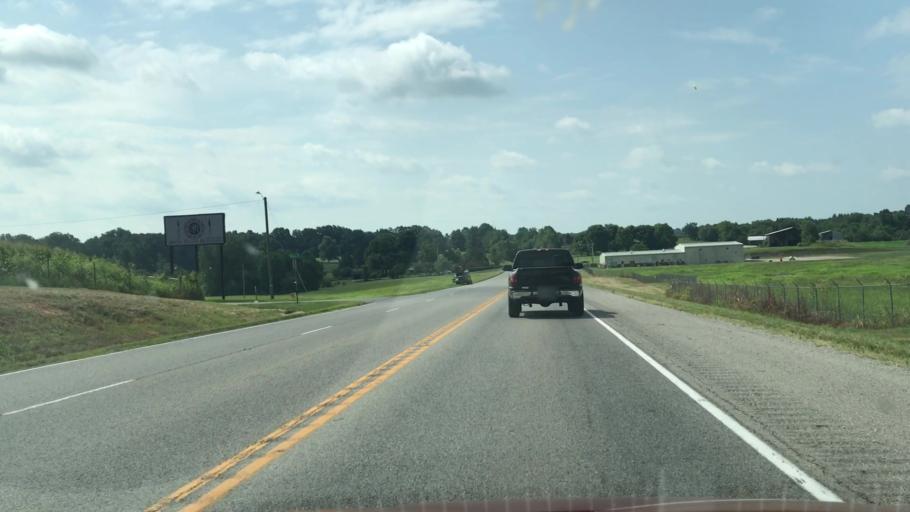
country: US
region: Kentucky
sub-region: Barren County
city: Glasgow
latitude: 37.0361
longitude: -85.9439
